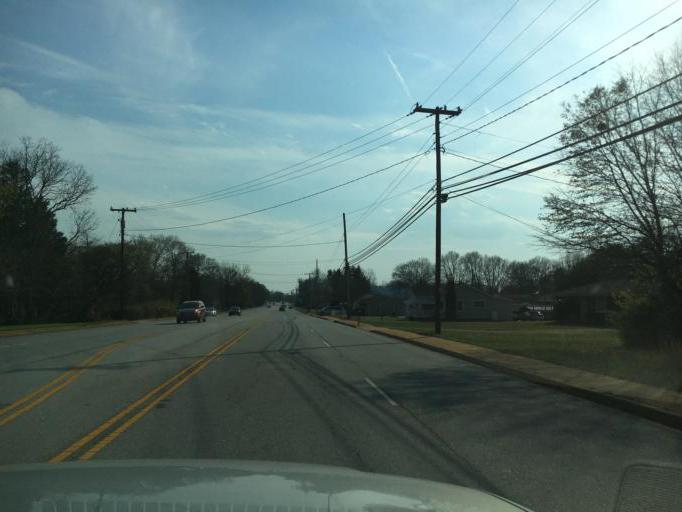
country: US
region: South Carolina
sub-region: Spartanburg County
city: Spartanburg
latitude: 35.0046
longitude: -81.9076
